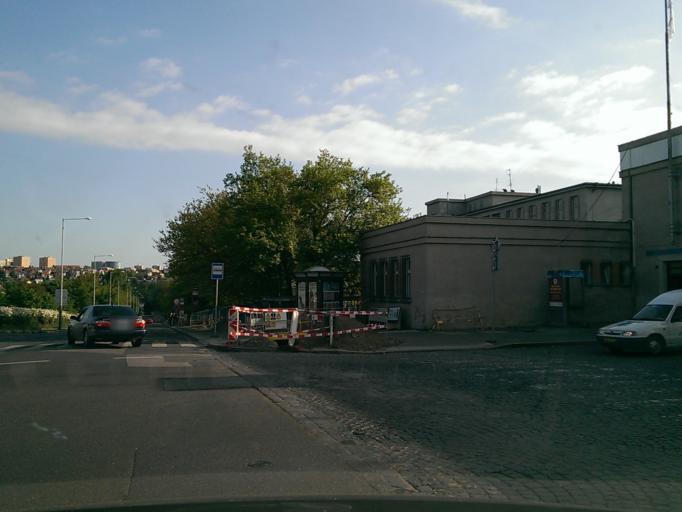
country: CZ
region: Praha
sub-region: Praha 4
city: Hodkovicky
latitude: 50.0299
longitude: 14.4561
